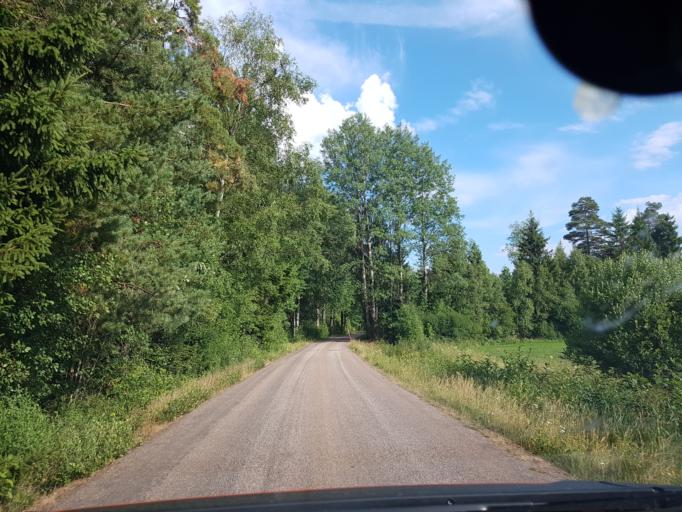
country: SE
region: Joenkoeping
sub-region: Gislaveds Kommun
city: Reftele
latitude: 57.2065
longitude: 13.5925
